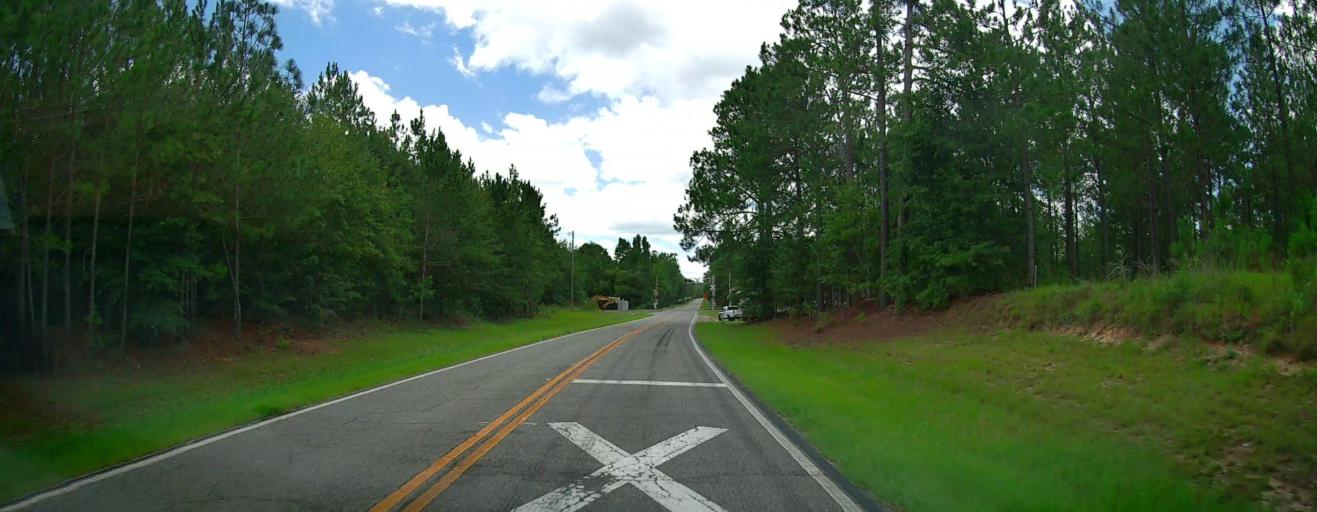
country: US
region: Georgia
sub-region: Wilcox County
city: Rochelle
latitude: 31.8601
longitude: -83.5583
